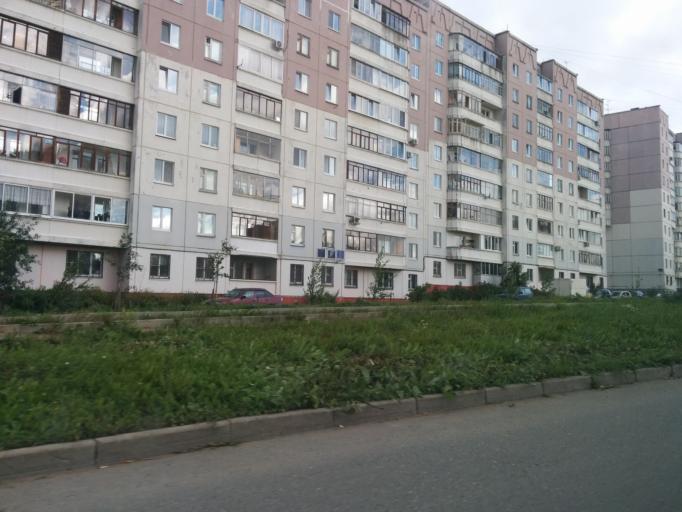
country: RU
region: Perm
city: Perm
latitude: 58.0038
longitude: 56.2974
